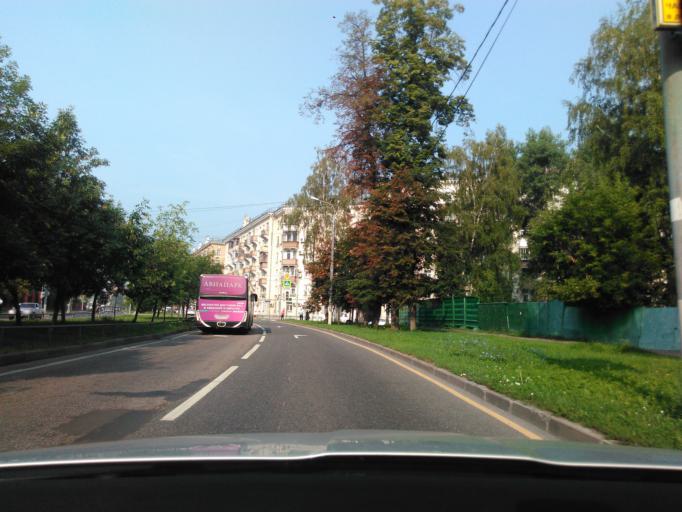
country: RU
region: Moscow
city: Sokol
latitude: 55.7937
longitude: 37.5199
